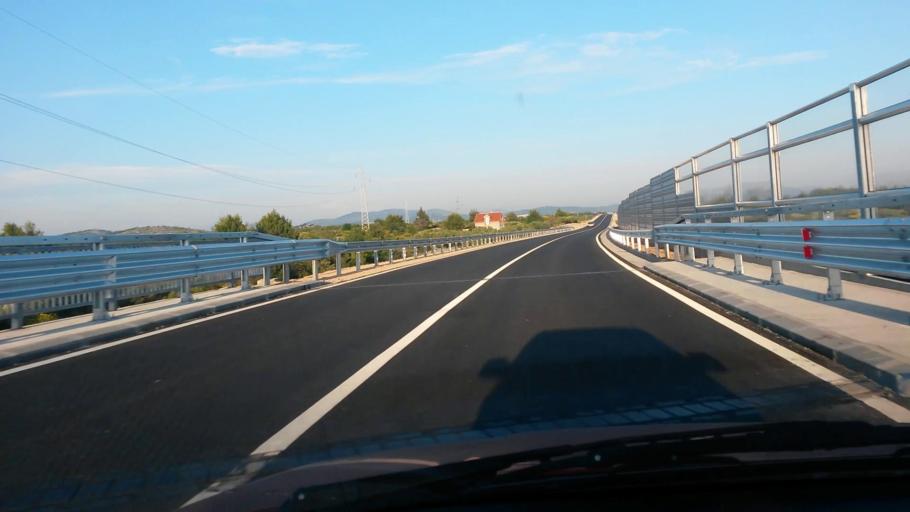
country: HR
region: Sibensko-Kniniska
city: Vodice
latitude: 43.7744
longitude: 15.7831
